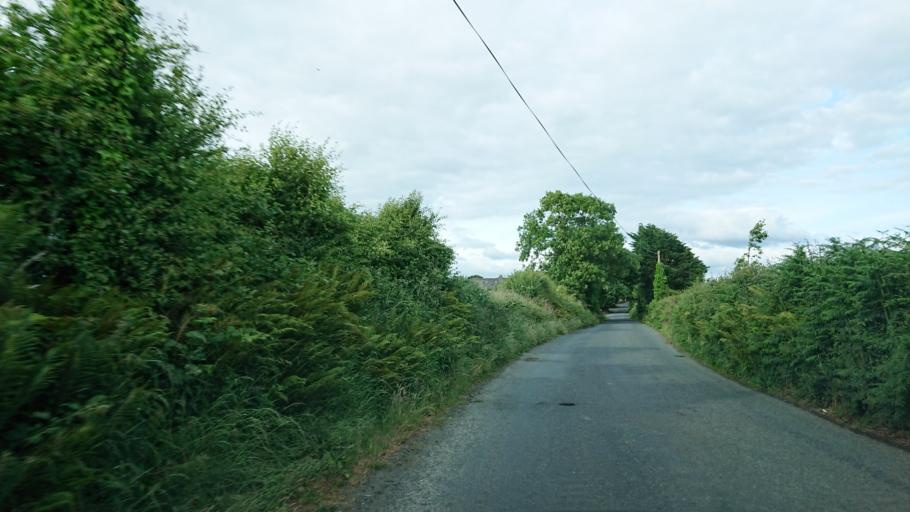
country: IE
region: Munster
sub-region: Waterford
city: Tra Mhor
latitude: 52.2101
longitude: -7.2063
